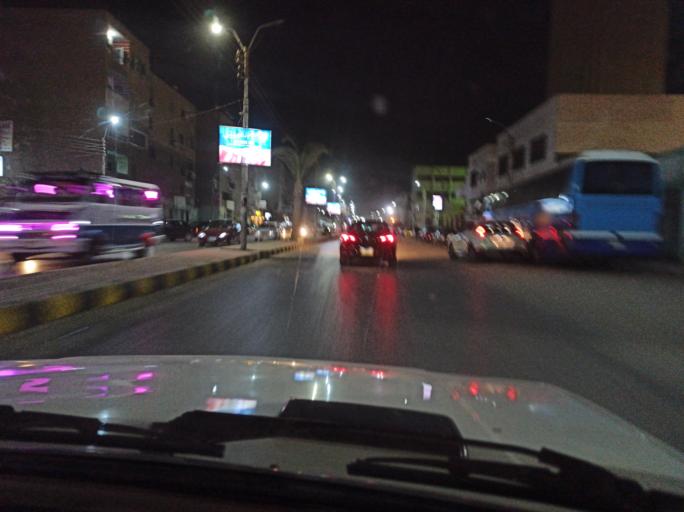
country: EG
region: Muhafazat Bani Suwayf
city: Bani Suwayf
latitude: 29.0731
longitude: 31.1123
